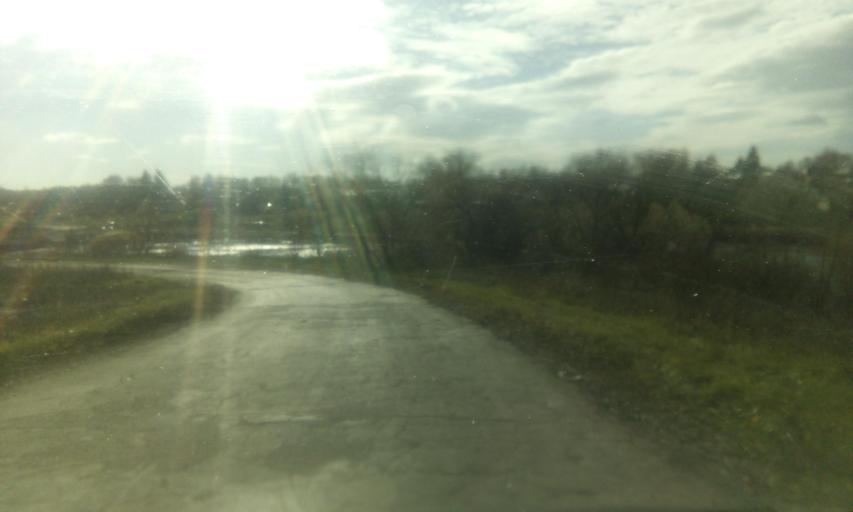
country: RU
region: Tula
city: Dubovka
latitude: 53.9496
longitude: 38.0278
